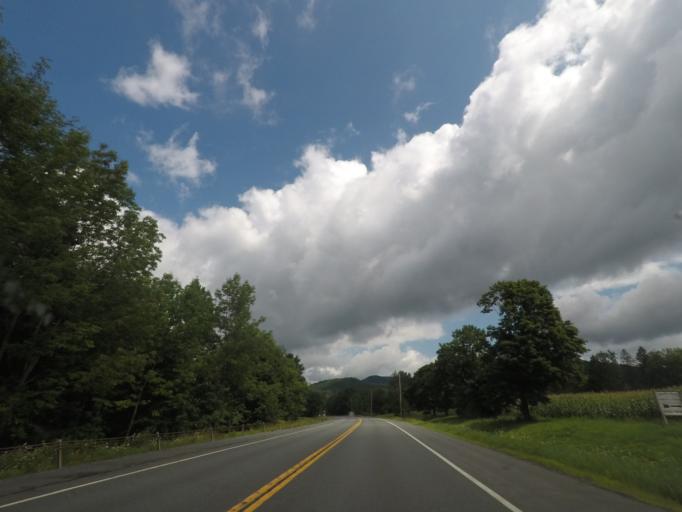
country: US
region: Massachusetts
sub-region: Berkshire County
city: Lanesborough
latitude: 42.6314
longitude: -73.3596
